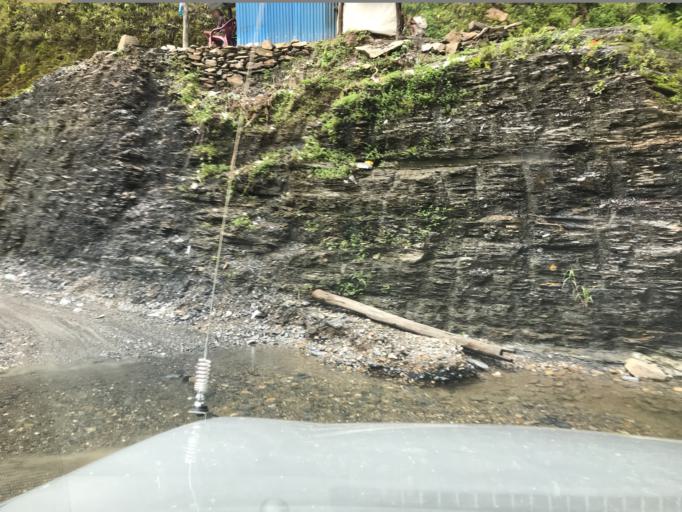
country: TL
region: Aileu
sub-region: Aileu Villa
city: Aileu
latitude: -8.6455
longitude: 125.5251
